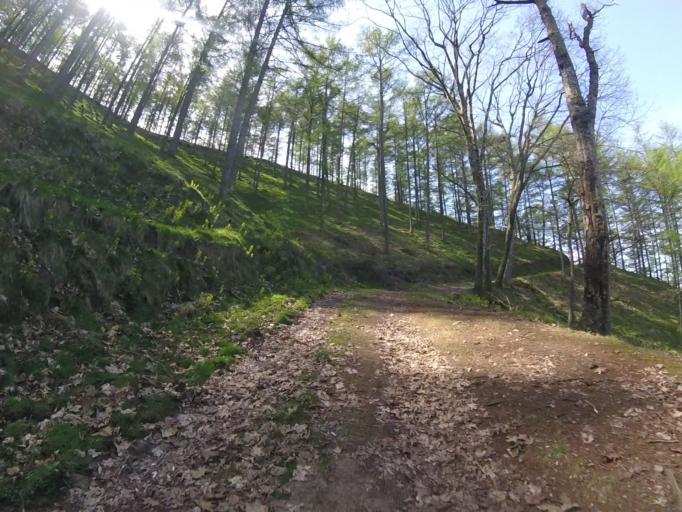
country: ES
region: Navarre
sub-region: Provincia de Navarra
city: Arano
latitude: 43.2570
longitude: -1.8308
